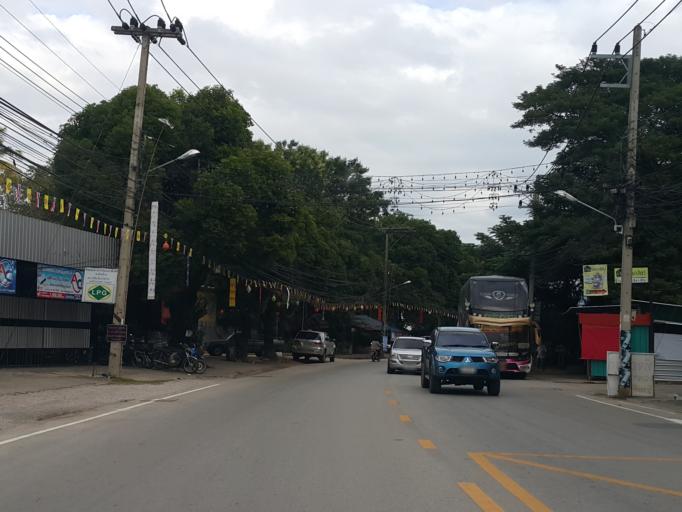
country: TH
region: Lampang
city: Lampang
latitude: 18.2898
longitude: 99.4801
